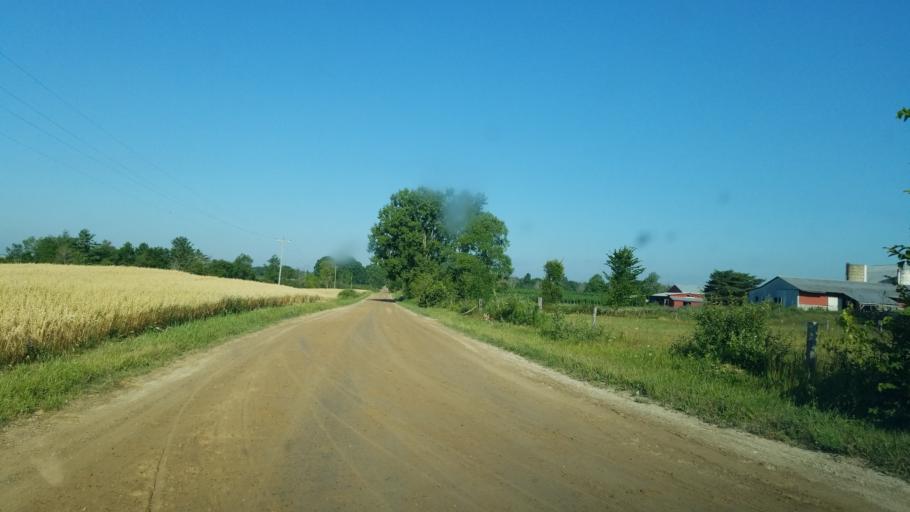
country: US
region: Michigan
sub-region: Mecosta County
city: Canadian Lakes
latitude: 43.5546
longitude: -85.3837
